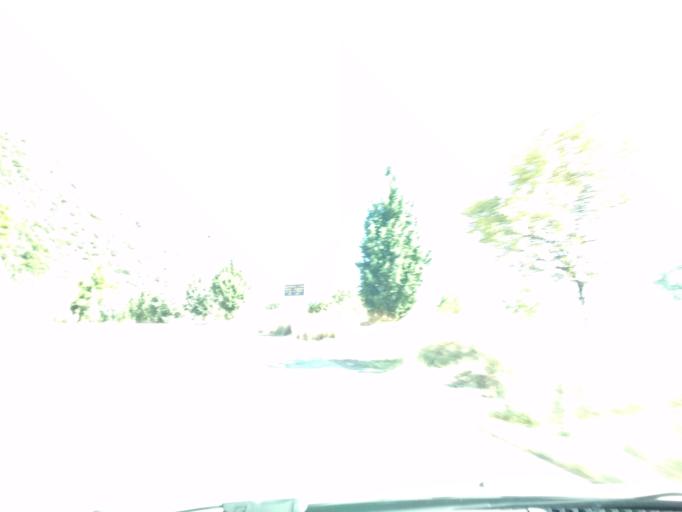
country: GR
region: Central Greece
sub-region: Nomos Evvoias
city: Oreoi
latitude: 38.8463
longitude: 23.0695
